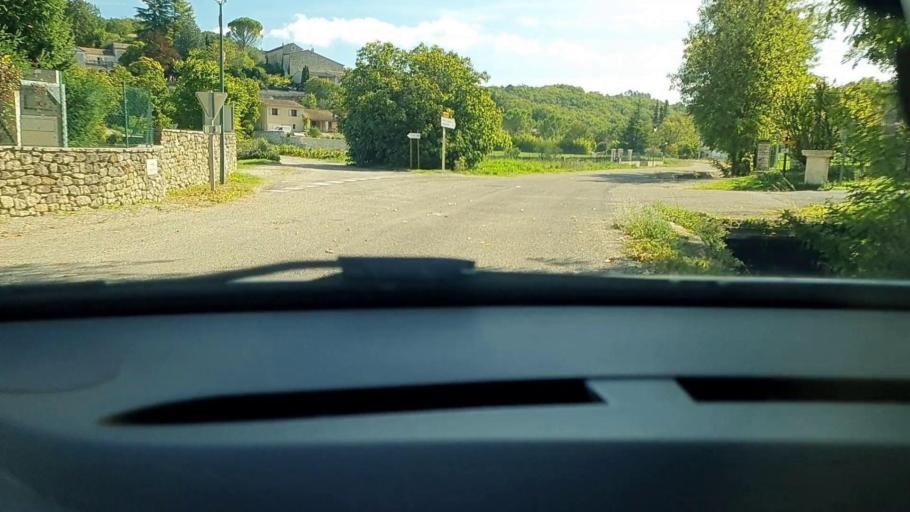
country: FR
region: Languedoc-Roussillon
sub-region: Departement du Gard
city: Saint-Ambroix
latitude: 44.2304
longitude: 4.2810
